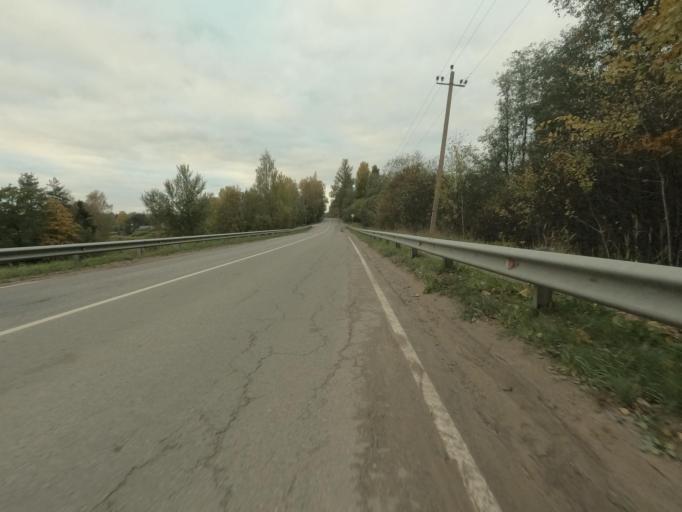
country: RU
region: Leningrad
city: Pavlovo
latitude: 59.7785
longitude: 30.9723
